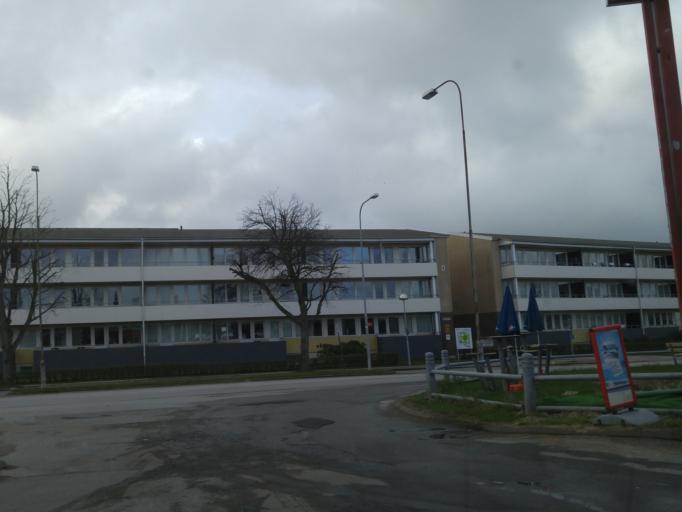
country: SE
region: Vaestra Goetaland
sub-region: Goteborg
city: Majorna
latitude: 57.6598
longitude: 11.8908
